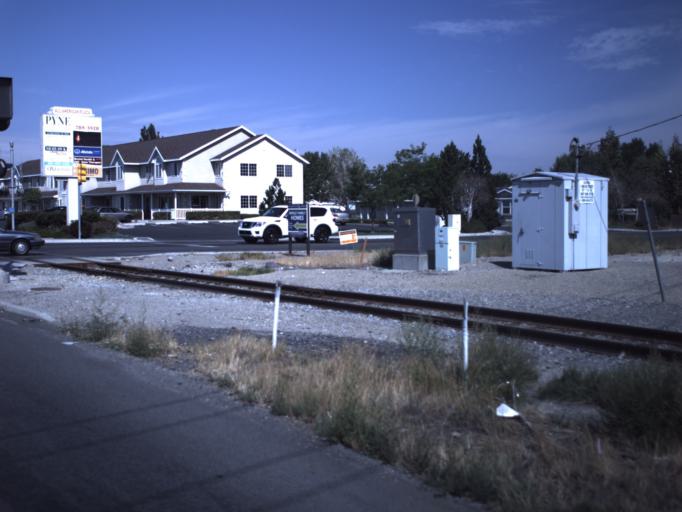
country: US
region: Utah
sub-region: Utah County
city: Pleasant Grove
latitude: 40.3680
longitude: -111.7593
